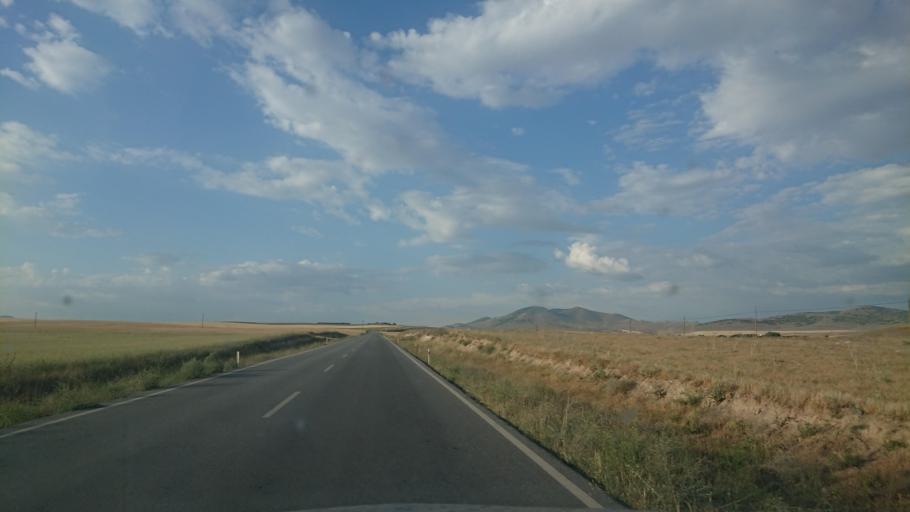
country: TR
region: Aksaray
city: Aksaray
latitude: 38.4907
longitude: 34.0701
